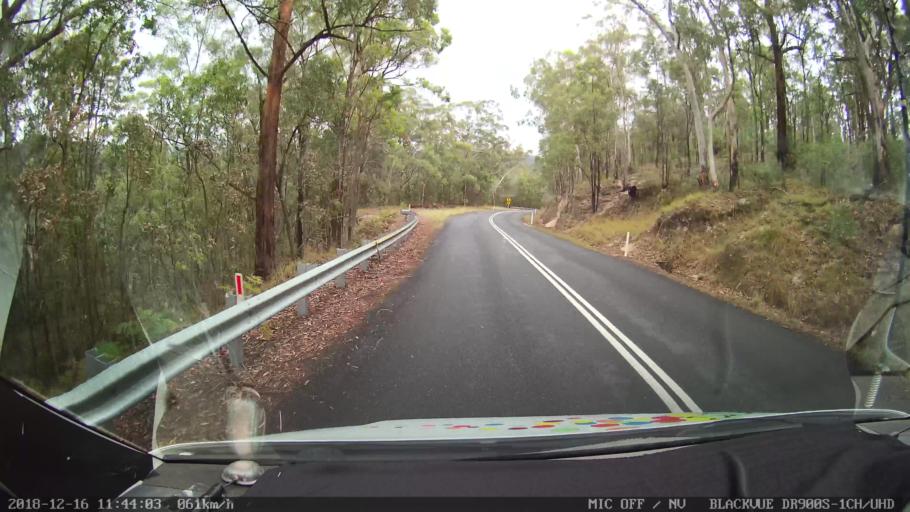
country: AU
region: New South Wales
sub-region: Tenterfield Municipality
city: Carrolls Creek
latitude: -28.9415
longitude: 152.2204
